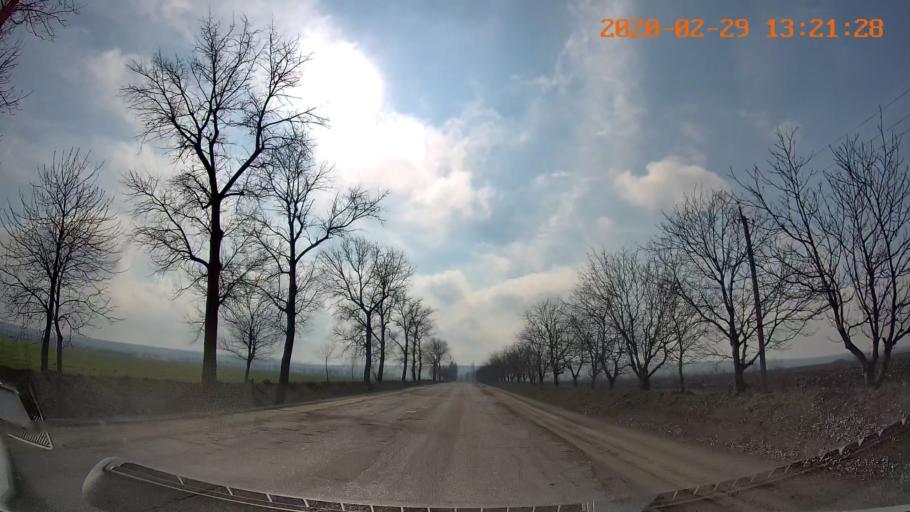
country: MD
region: Telenesti
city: Camenca
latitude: 47.9700
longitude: 28.6327
